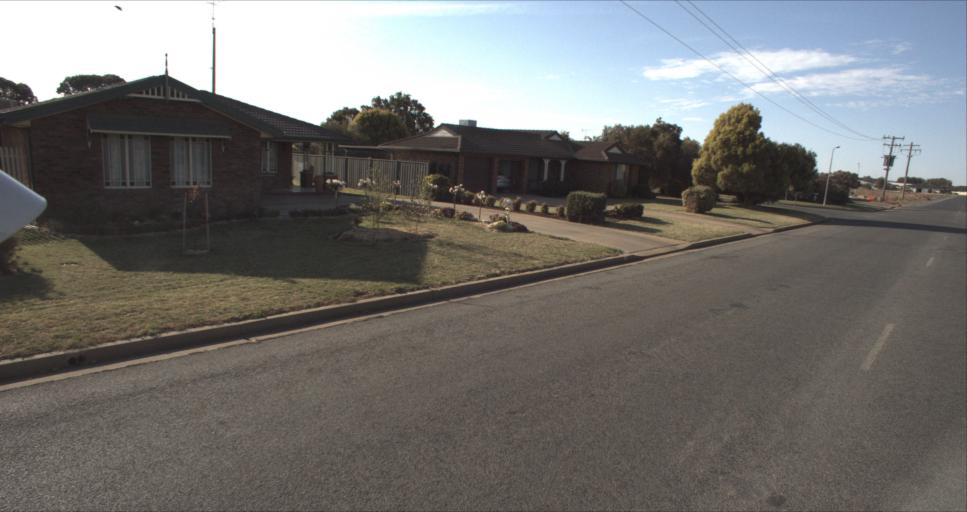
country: AU
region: New South Wales
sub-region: Leeton
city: Leeton
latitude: -34.5455
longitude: 146.3989
